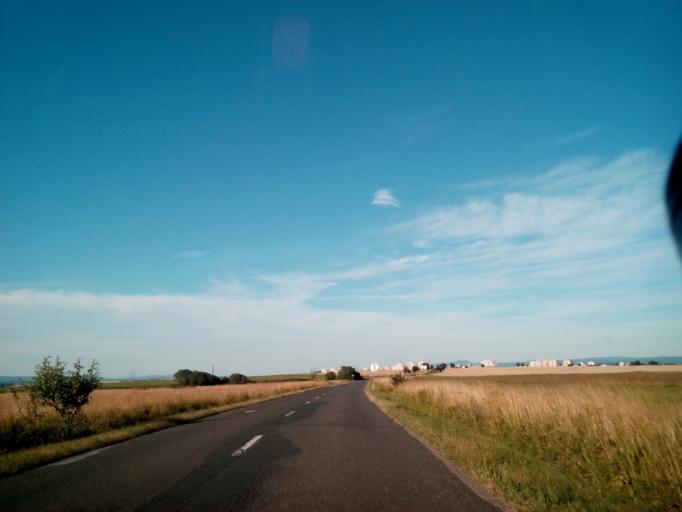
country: SK
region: Presovsky
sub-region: Okres Poprad
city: Poprad
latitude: 49.0351
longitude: 20.2663
